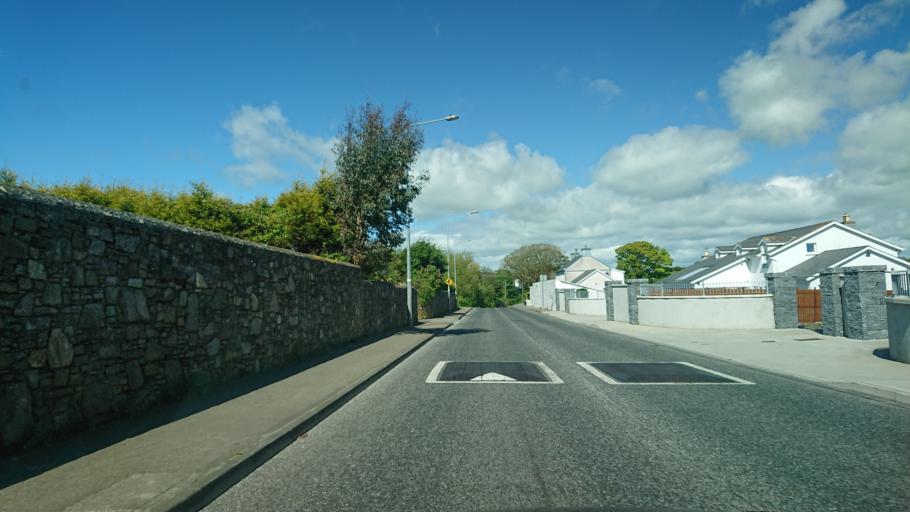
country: IE
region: Munster
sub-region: Waterford
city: Waterford
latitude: 52.2646
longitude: -7.1341
